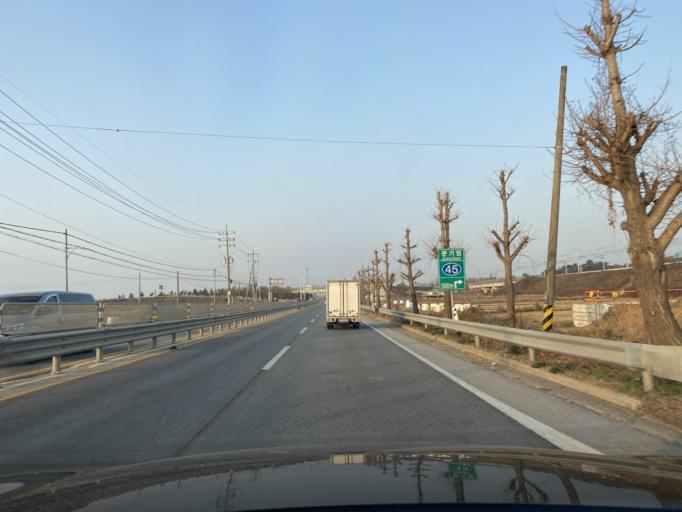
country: KR
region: Chungcheongnam-do
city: Yesan
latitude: 36.7005
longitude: 126.8295
